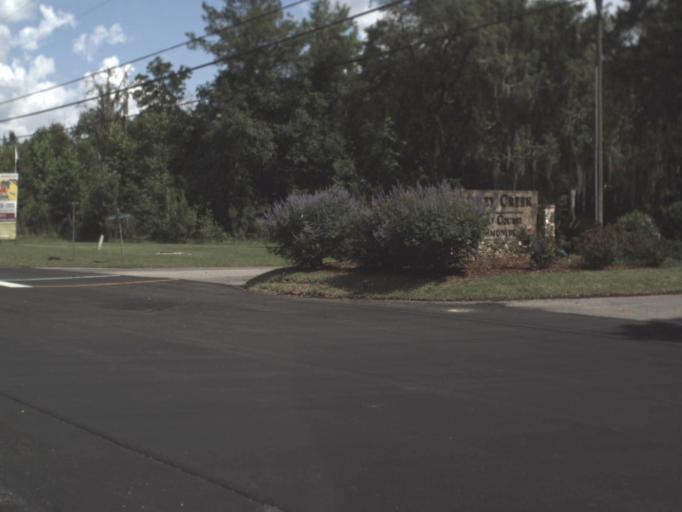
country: US
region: Florida
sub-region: Alachua County
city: Alachua
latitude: 29.7657
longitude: -82.4115
